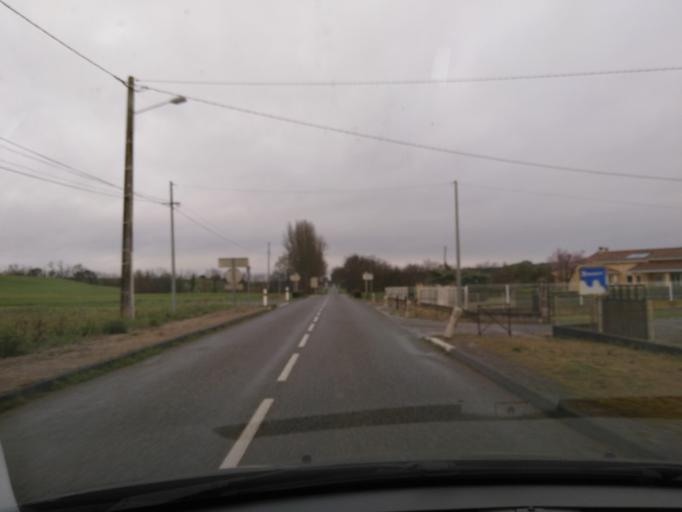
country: FR
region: Midi-Pyrenees
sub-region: Departement de la Haute-Garonne
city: Montesquieu-Volvestre
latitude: 43.1855
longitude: 1.2404
